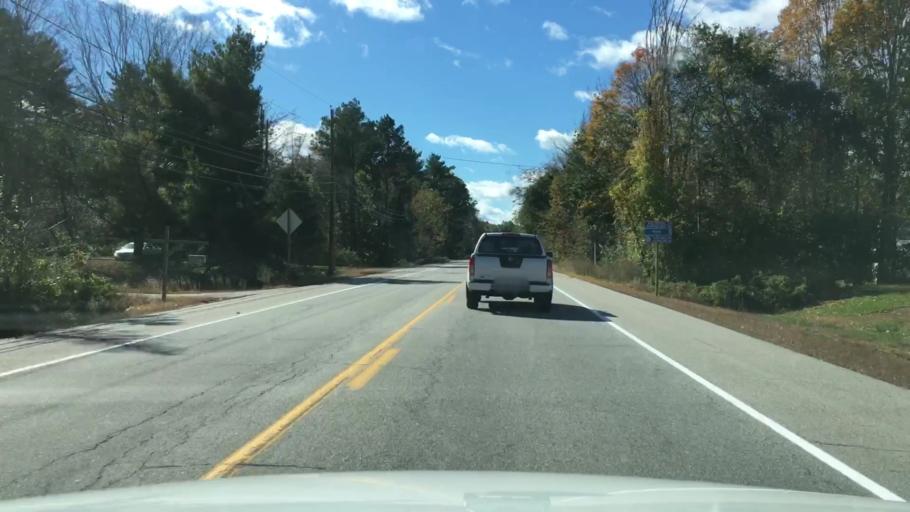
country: US
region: Maine
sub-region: York County
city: Alfred
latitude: 43.4737
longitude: -70.7144
